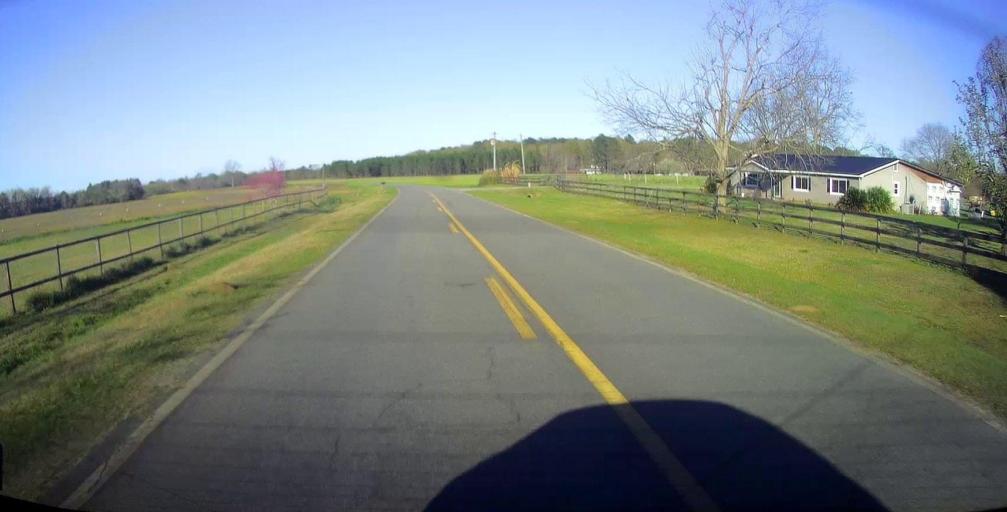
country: US
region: Georgia
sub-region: Pulaski County
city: Hawkinsville
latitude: 32.3137
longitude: -83.5748
